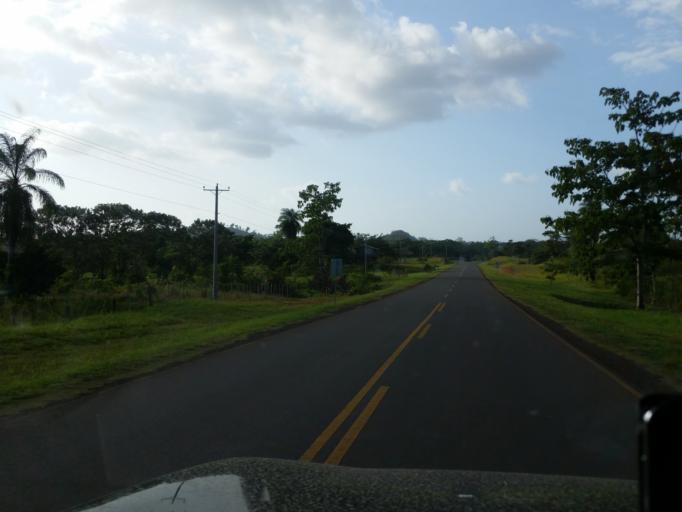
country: NI
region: Rio San Juan
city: San Carlos
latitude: 11.1668
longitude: -84.6674
